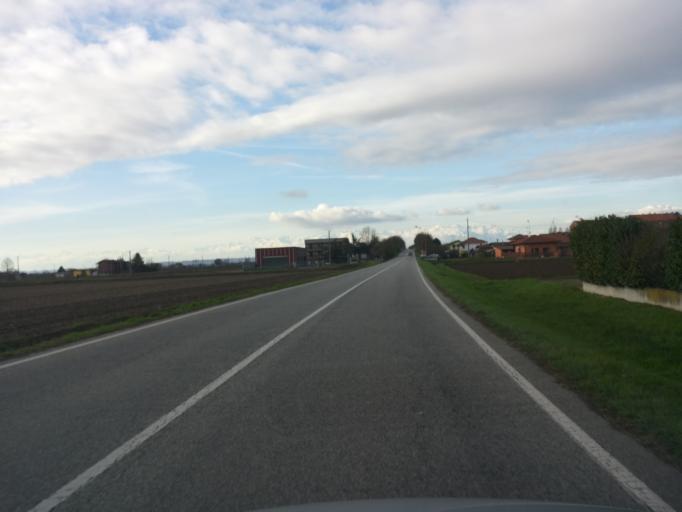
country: IT
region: Piedmont
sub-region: Provincia di Vercelli
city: Tronzano Vercellese
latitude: 45.3382
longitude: 8.1721
